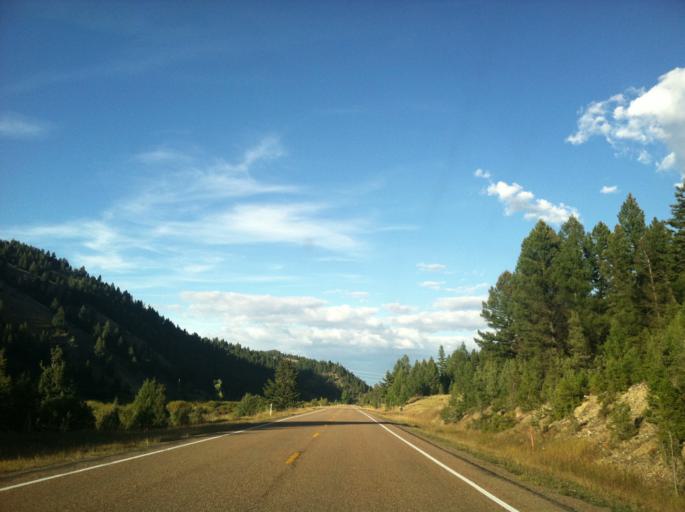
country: US
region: Montana
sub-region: Granite County
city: Philipsburg
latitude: 46.4323
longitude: -113.2700
